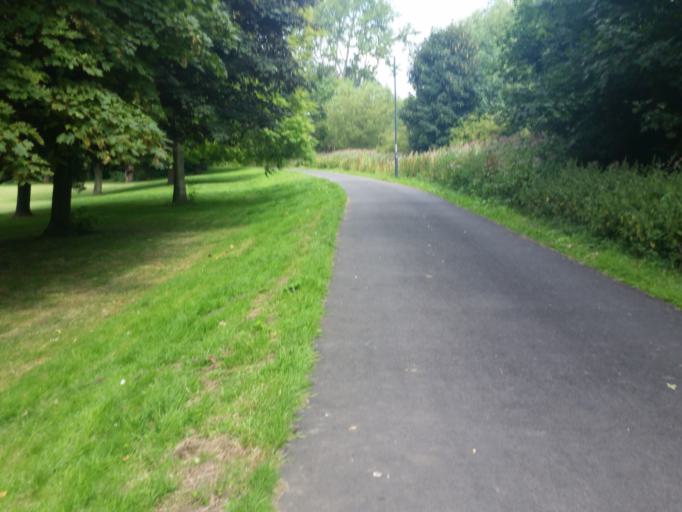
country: GB
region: England
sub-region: Derby
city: Derby
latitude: 52.9073
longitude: -1.4365
